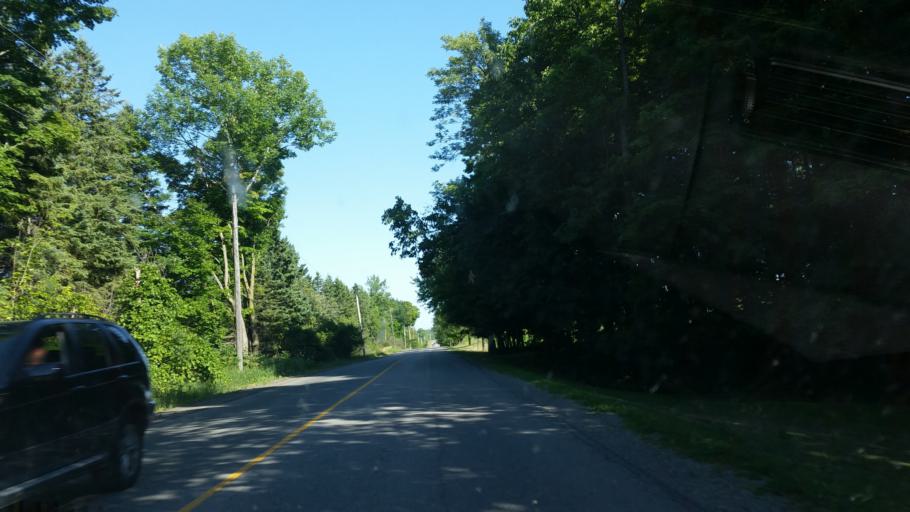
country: CA
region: Ontario
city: Bradford West Gwillimbury
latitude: 43.9527
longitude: -79.7670
